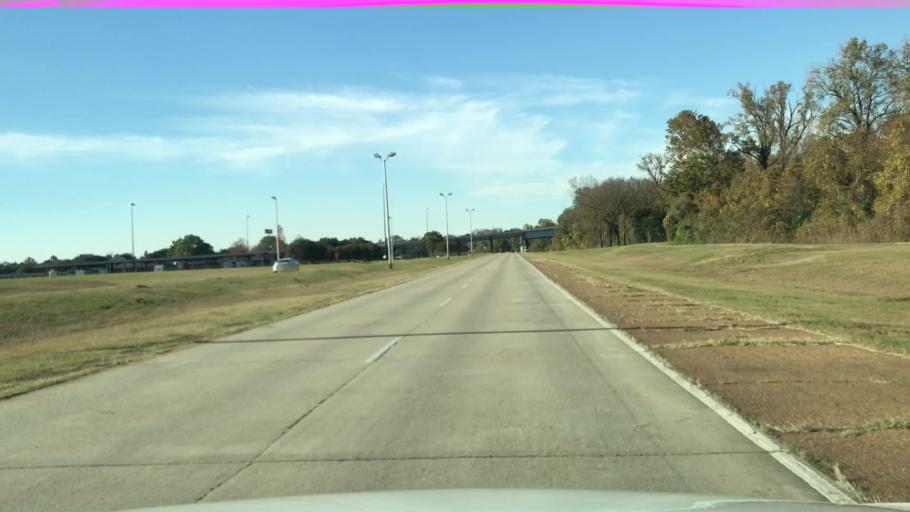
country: US
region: Louisiana
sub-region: Bossier Parish
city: Bossier City
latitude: 32.4876
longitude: -93.6972
